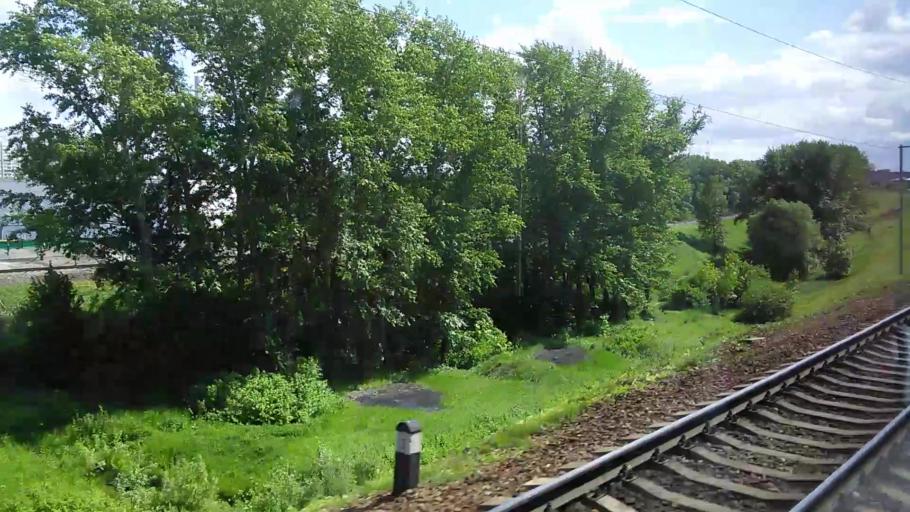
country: RU
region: Moscow
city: Likhobory
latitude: 55.8560
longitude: 37.5732
